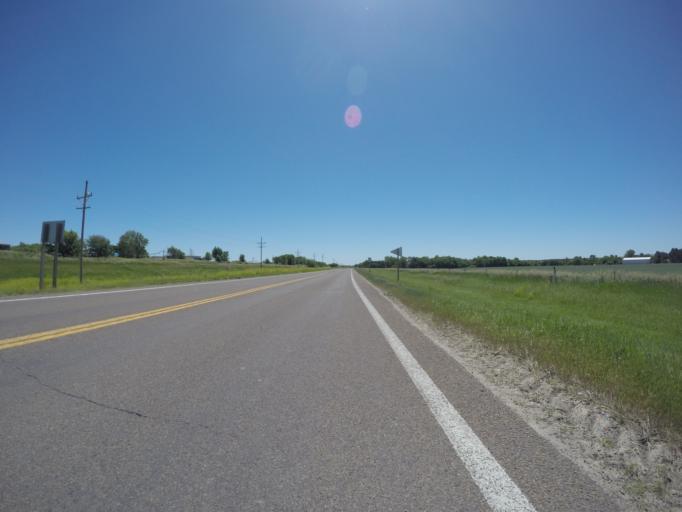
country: US
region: Kansas
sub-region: Phillips County
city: Phillipsburg
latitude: 39.8271
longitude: -99.5698
